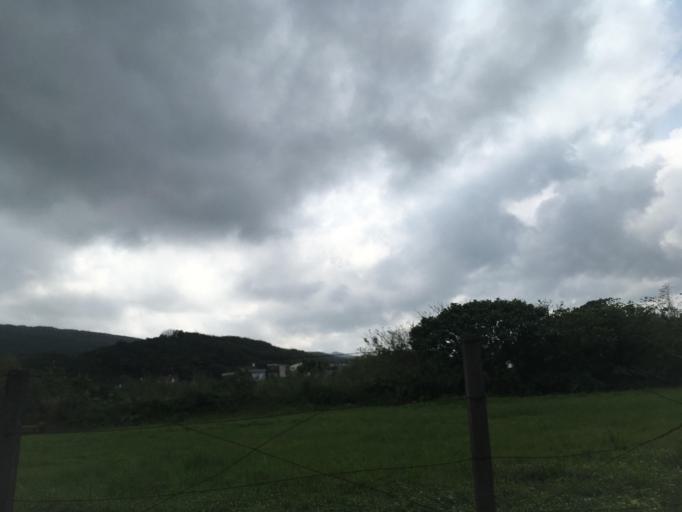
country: TW
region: Taiwan
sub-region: Keelung
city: Keelung
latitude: 25.0168
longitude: 121.9484
